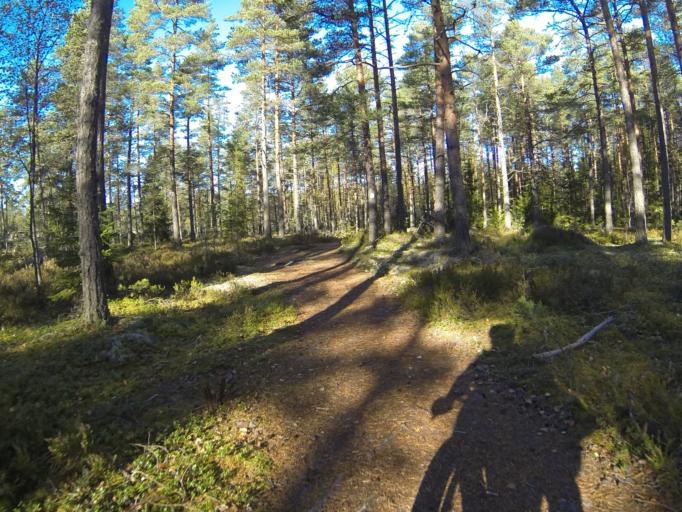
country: FI
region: Varsinais-Suomi
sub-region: Salo
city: Saerkisalo
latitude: 60.2058
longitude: 22.9210
